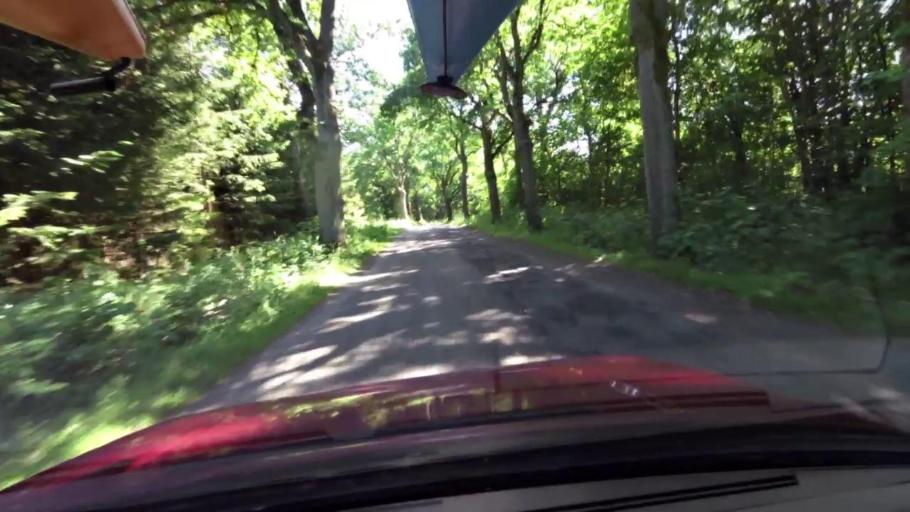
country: PL
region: Pomeranian Voivodeship
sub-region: Powiat slupski
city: Kepice
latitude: 54.1874
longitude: 16.8903
